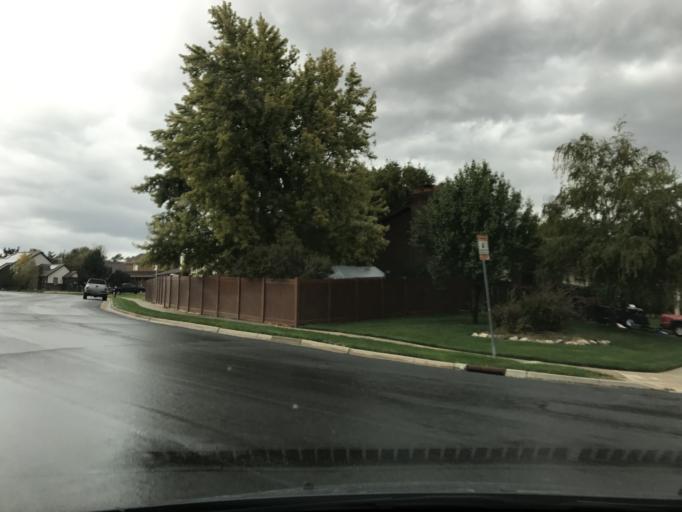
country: US
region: Utah
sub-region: Davis County
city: South Weber
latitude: 41.1108
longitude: -111.9146
